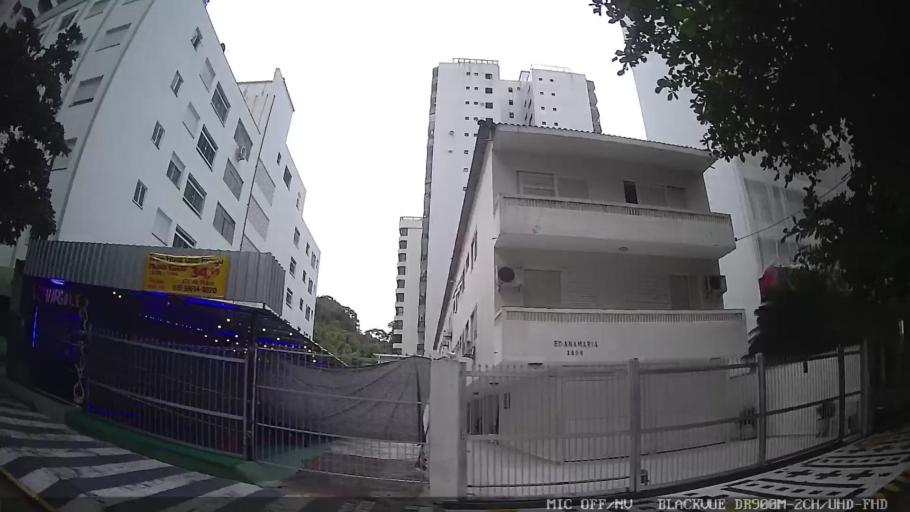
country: BR
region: Sao Paulo
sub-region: Guaruja
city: Guaruja
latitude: -24.0011
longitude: -46.2666
